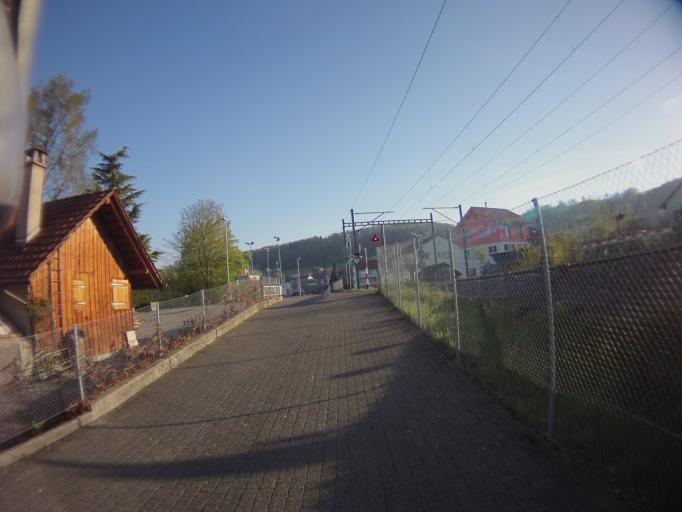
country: CH
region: Zurich
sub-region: Bezirk Affoltern
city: Affoltern / Unterdorf
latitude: 47.2827
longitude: 8.4515
